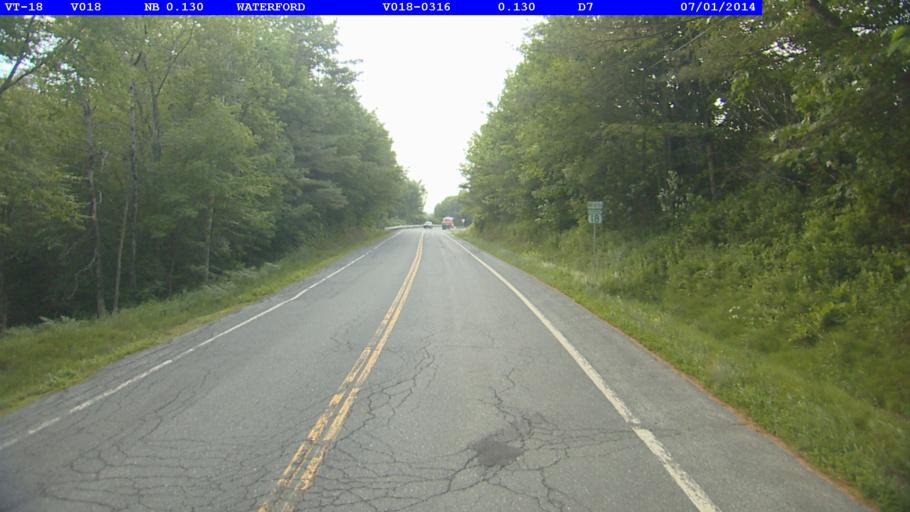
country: US
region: New Hampshire
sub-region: Grafton County
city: Littleton
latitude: 44.3449
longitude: -71.8898
